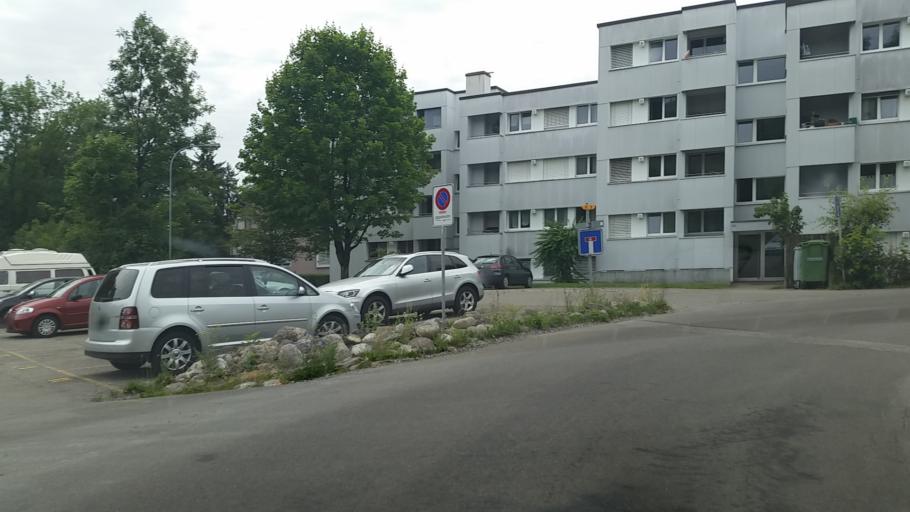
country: CH
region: Zurich
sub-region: Bezirk Dielsdorf
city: Sonnhalde
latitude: 47.4607
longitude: 8.4434
